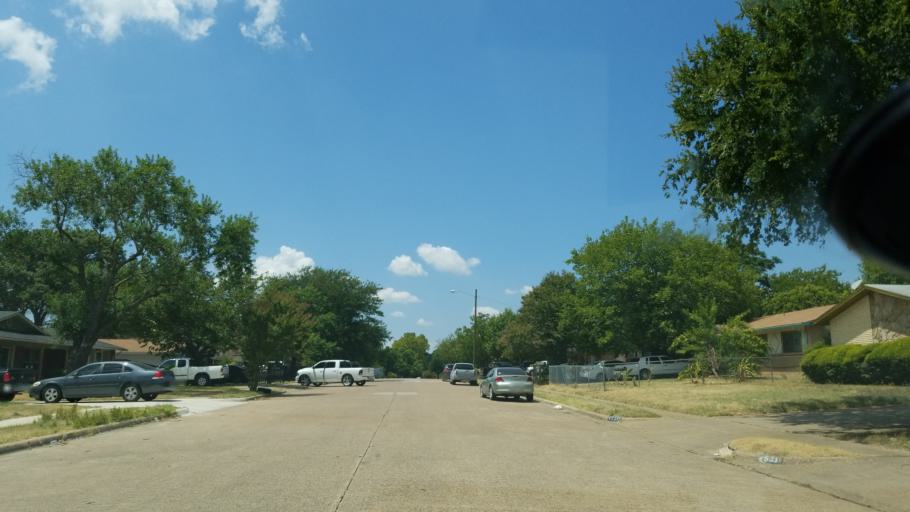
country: US
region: Texas
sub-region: Dallas County
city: Cockrell Hill
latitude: 32.7135
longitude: -96.8936
